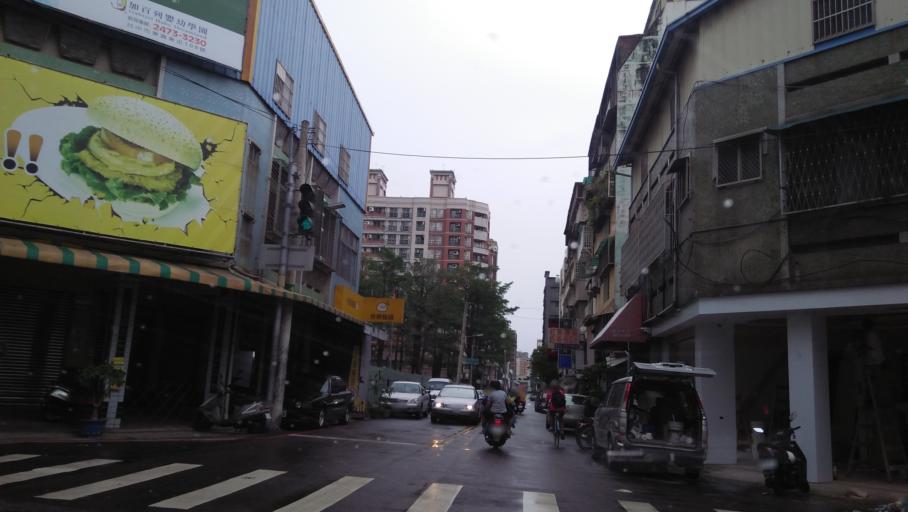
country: TW
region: Taiwan
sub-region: Taichung City
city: Taichung
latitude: 24.1380
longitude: 120.6617
